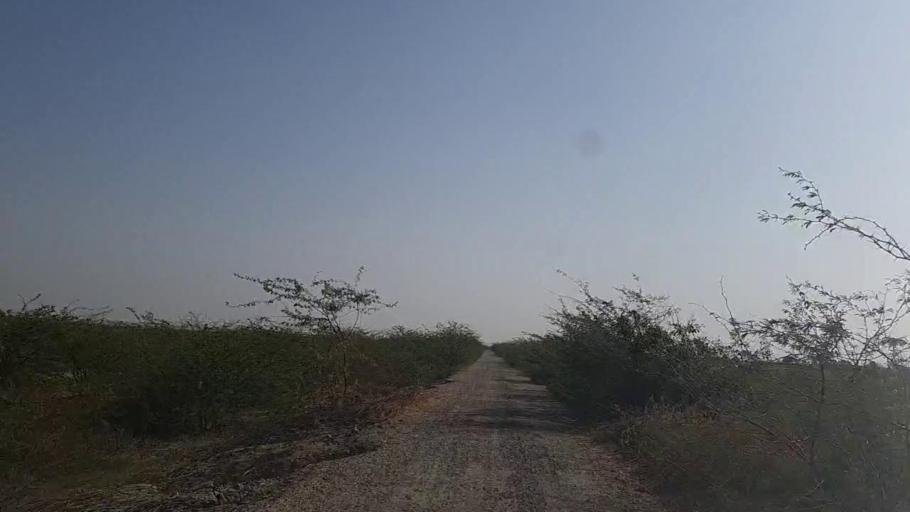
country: PK
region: Sindh
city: Kadhan
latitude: 24.5905
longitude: 69.2627
